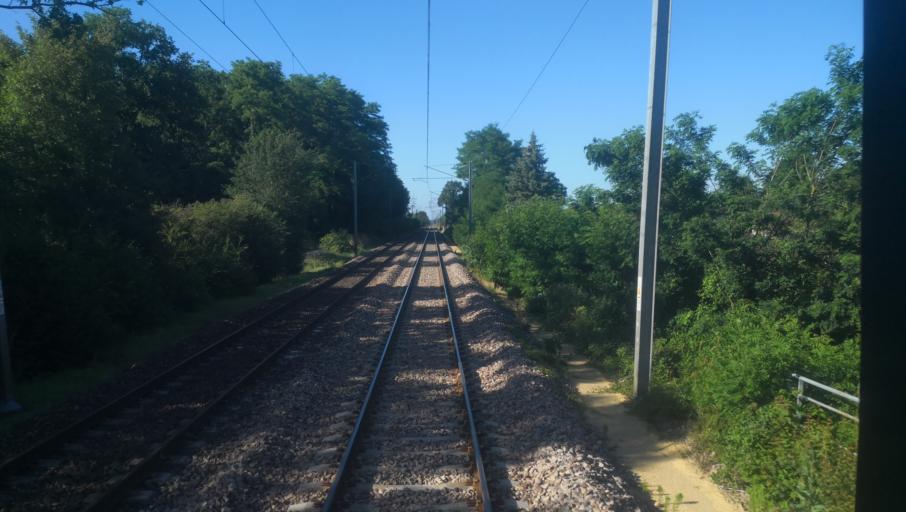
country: FR
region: Bourgogne
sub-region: Departement de la Nievre
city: Cosne-Cours-sur-Loire
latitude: 47.3735
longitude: 2.9008
